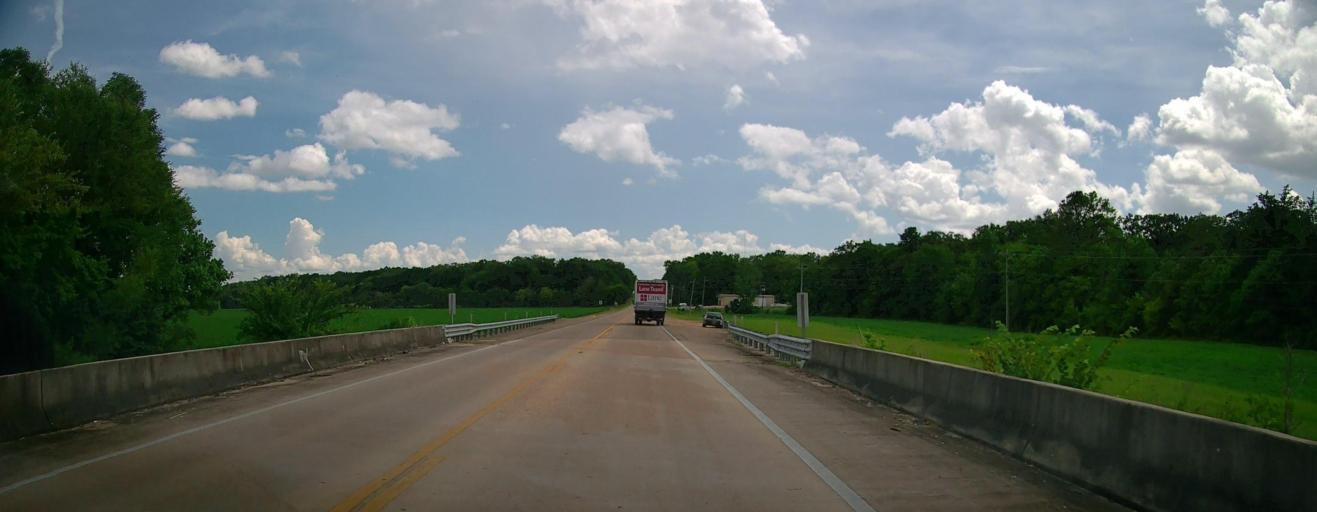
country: US
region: Mississippi
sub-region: Lee County
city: Shannon
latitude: 34.1375
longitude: -88.7194
